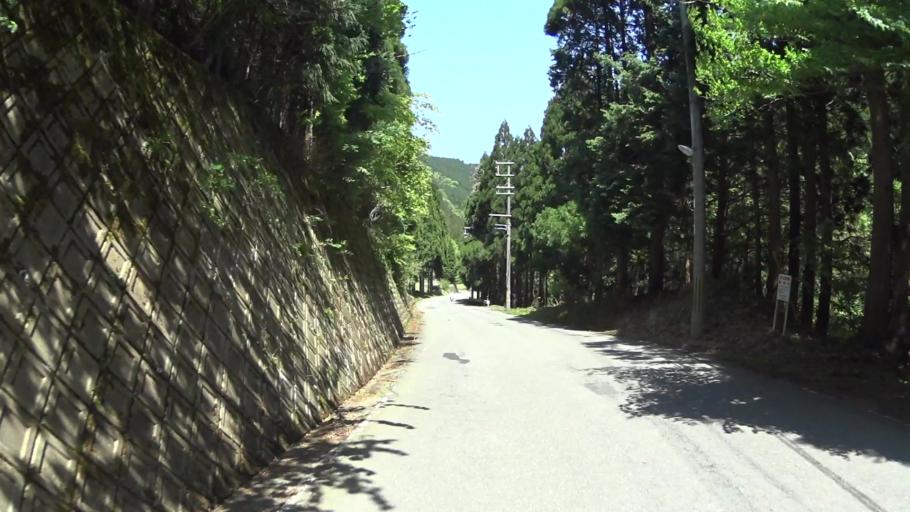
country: JP
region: Shiga Prefecture
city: Kitahama
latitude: 35.1816
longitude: 135.7863
